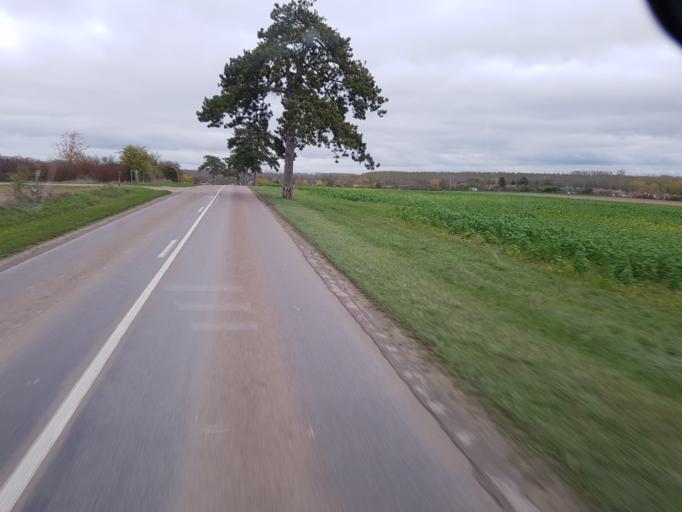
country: FR
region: Champagne-Ardenne
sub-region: Departement de l'Aube
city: Mery-sur-Seine
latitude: 48.4826
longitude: 3.8792
